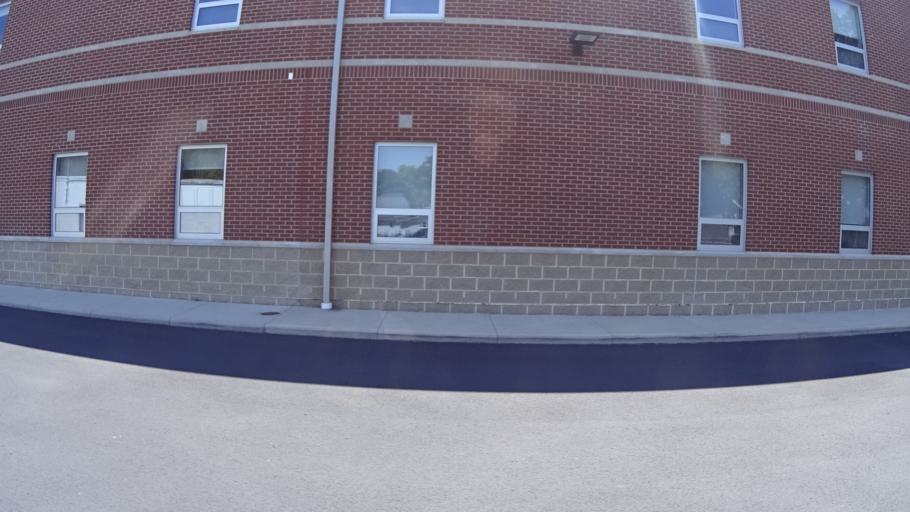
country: US
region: Ohio
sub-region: Erie County
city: Sandusky
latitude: 41.3992
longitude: -82.8023
